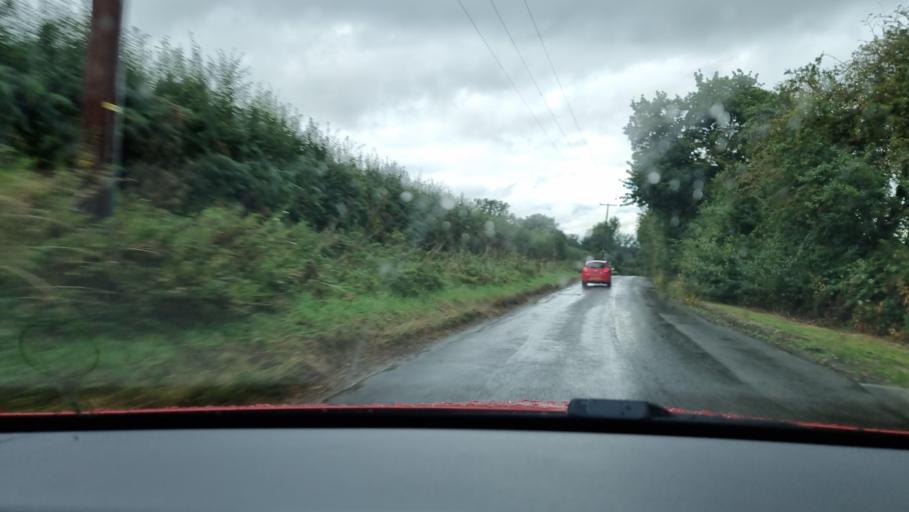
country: GB
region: England
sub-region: Buckinghamshire
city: Chesham
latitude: 51.7226
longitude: -0.5801
